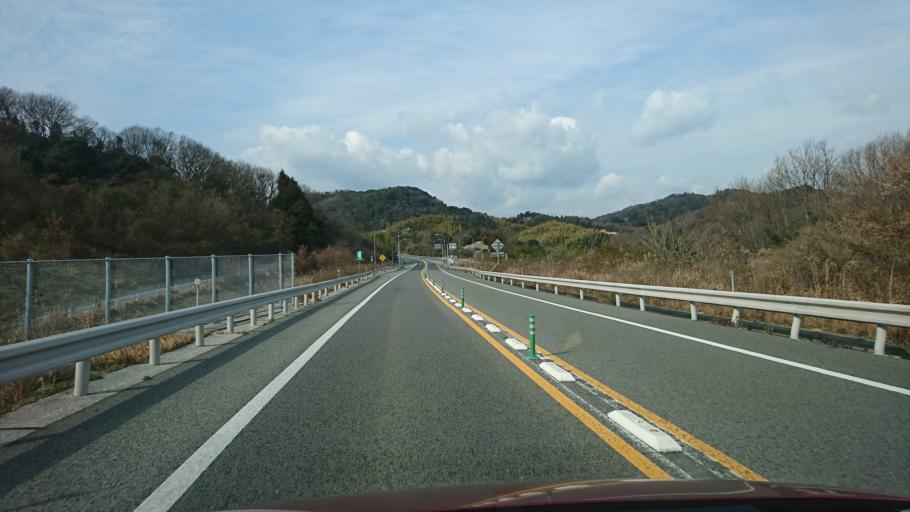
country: JP
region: Hiroshima
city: Innoshima
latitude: 34.1290
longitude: 133.0335
